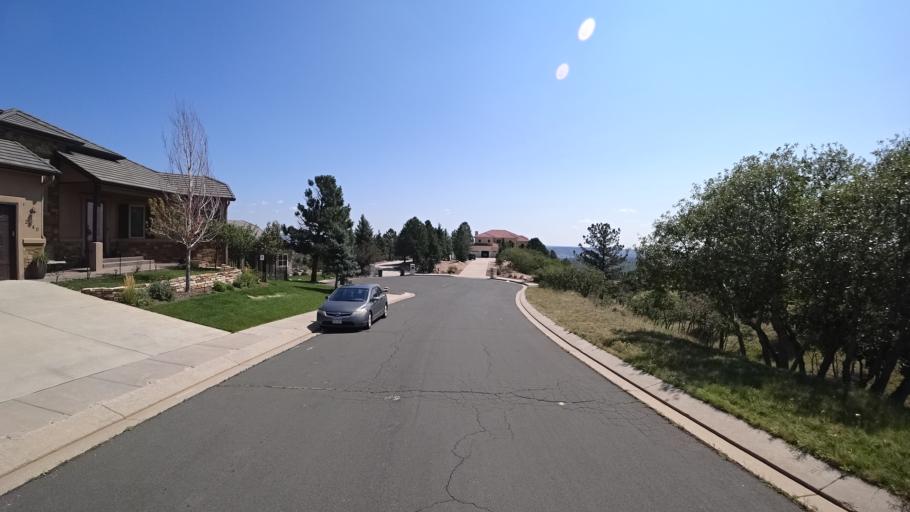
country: US
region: Colorado
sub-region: El Paso County
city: Air Force Academy
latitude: 38.9241
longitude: -104.8759
